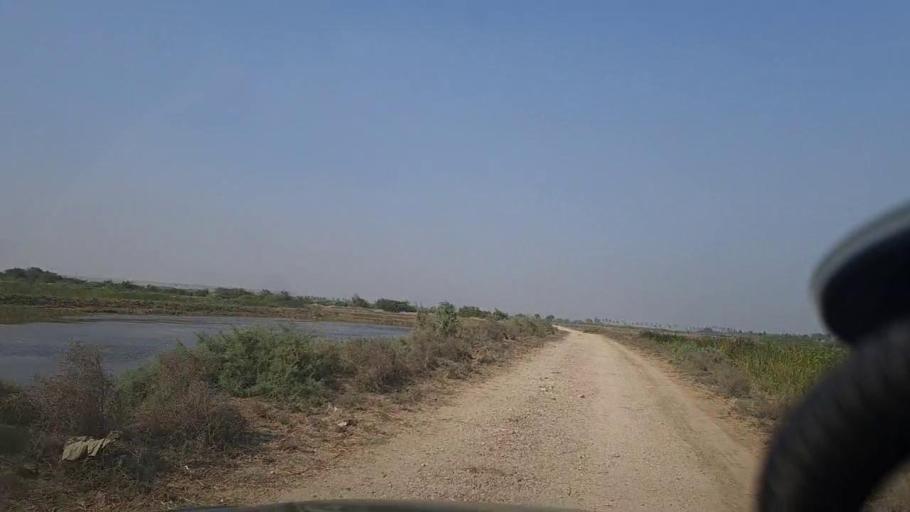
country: PK
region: Sindh
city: Thatta
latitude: 24.6167
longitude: 67.8842
